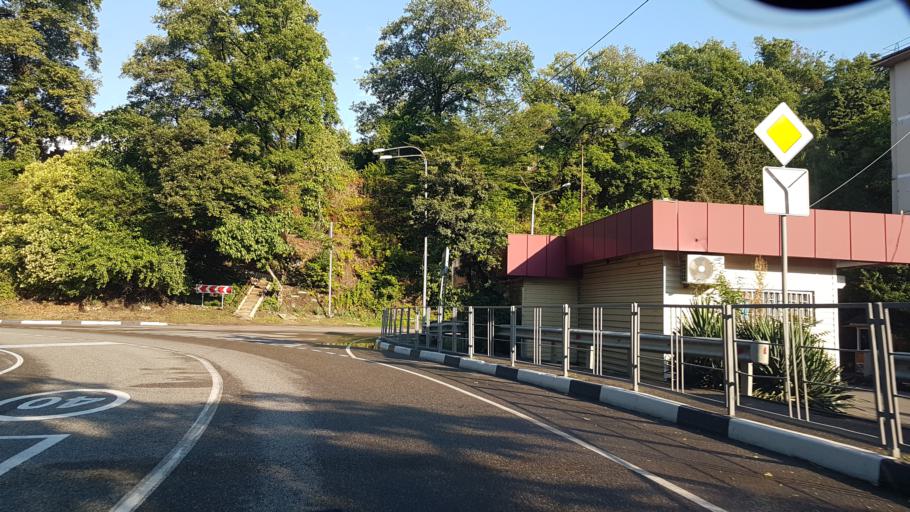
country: RU
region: Krasnodarskiy
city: Vardane
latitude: 43.7998
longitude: 39.4693
